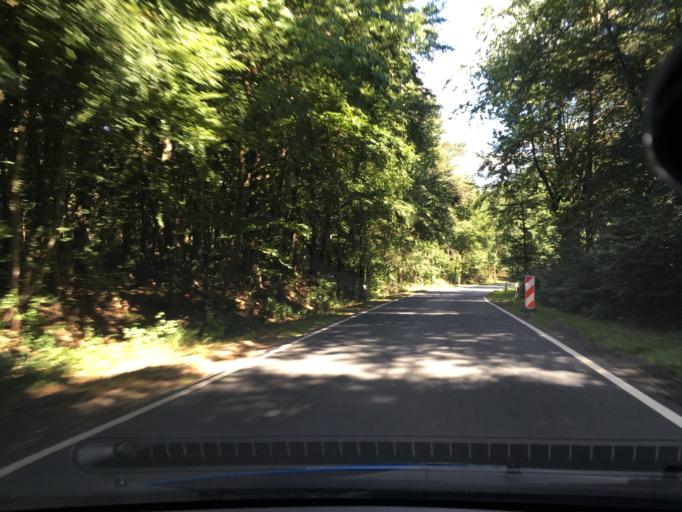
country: DE
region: Lower Saxony
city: Tosterglope
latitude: 53.2078
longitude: 10.8473
